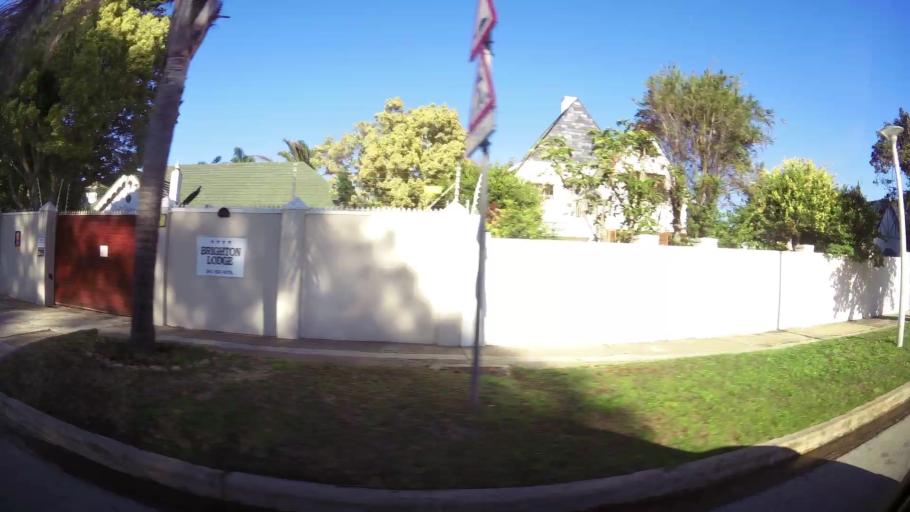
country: ZA
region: Eastern Cape
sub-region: Nelson Mandela Bay Metropolitan Municipality
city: Port Elizabeth
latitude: -33.9857
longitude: 25.6637
